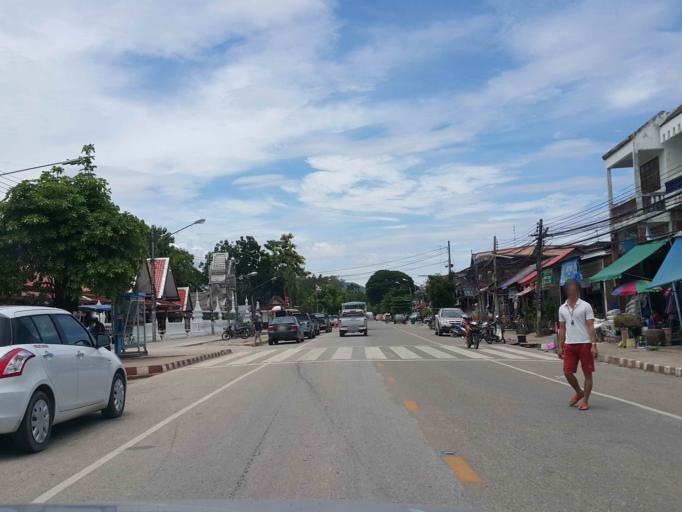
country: TH
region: Sukhothai
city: Ban Na
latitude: 17.0185
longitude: 99.7110
